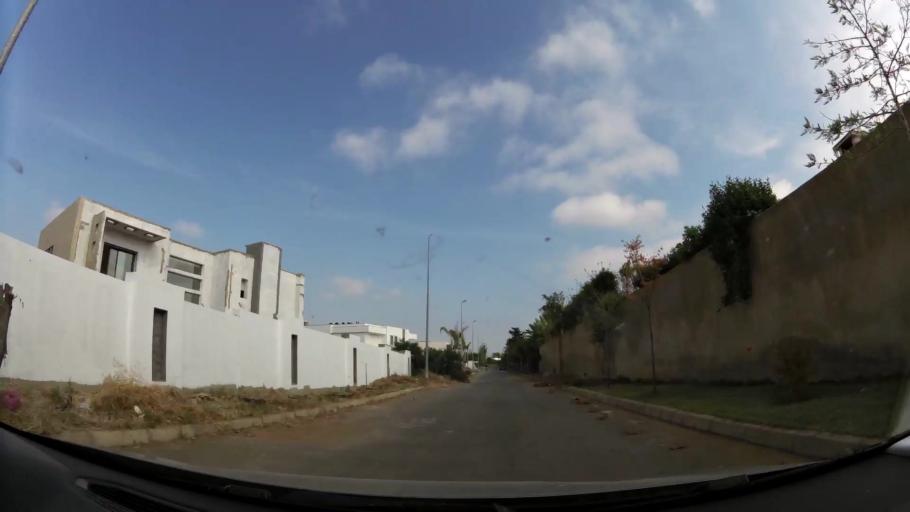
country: MA
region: Rabat-Sale-Zemmour-Zaer
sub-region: Rabat
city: Rabat
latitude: 33.9624
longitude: -6.8405
